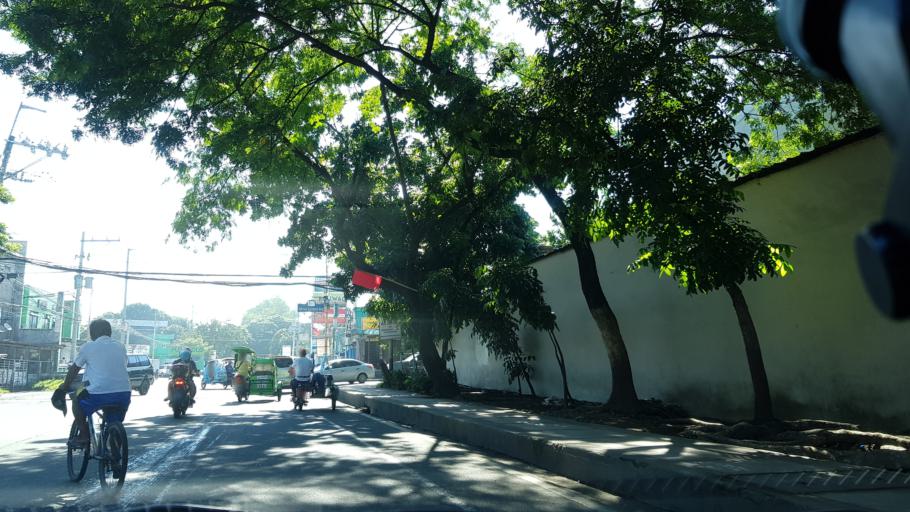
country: PH
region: Calabarzon
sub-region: Province of Rizal
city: Cainta
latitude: 14.5671
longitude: 121.0939
